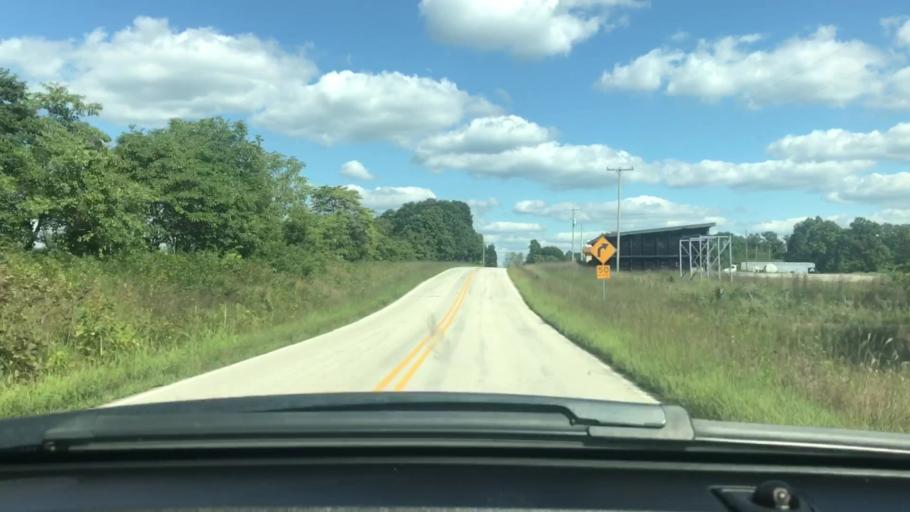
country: US
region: Missouri
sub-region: Wright County
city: Hartville
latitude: 37.3769
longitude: -92.4101
